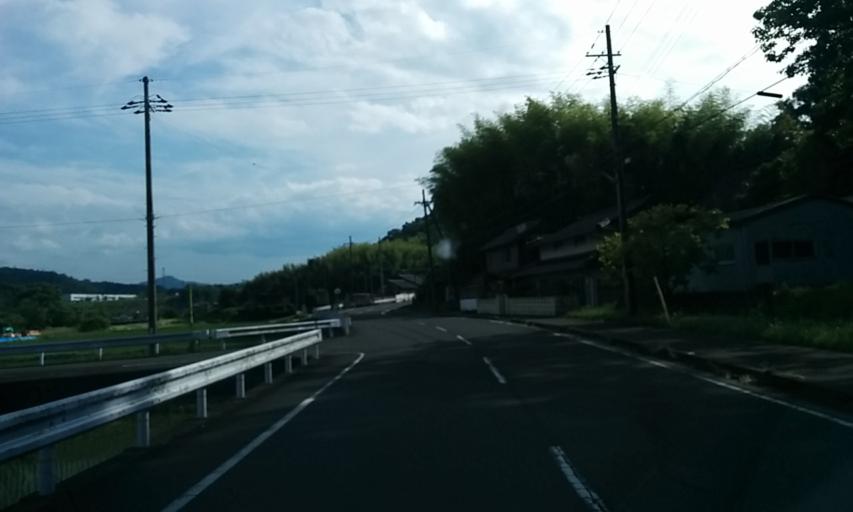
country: JP
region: Kyoto
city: Ayabe
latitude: 35.3372
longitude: 135.3031
